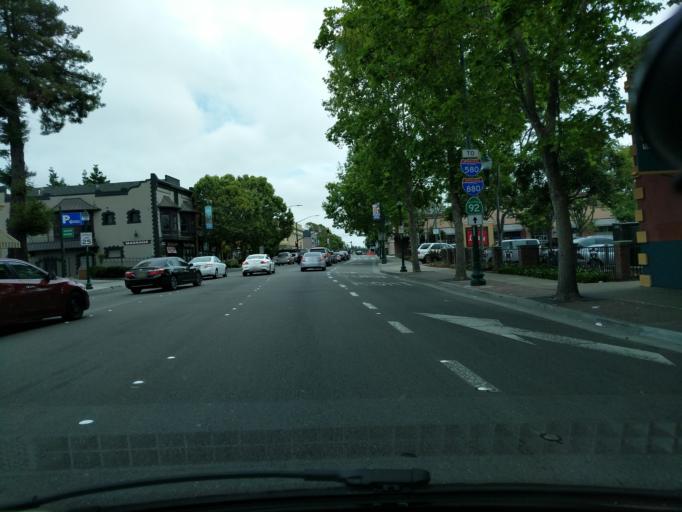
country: US
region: California
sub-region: Alameda County
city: Hayward
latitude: 37.6729
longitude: -122.0848
